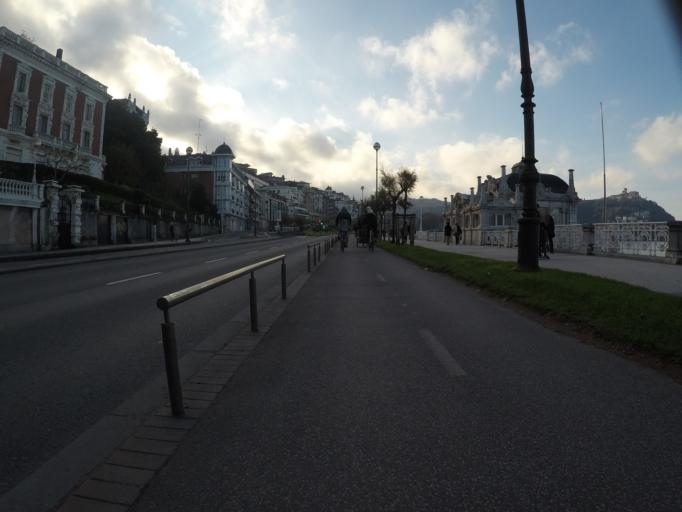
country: ES
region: Basque Country
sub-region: Provincia de Guipuzcoa
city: San Sebastian
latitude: 43.3149
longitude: -1.9901
